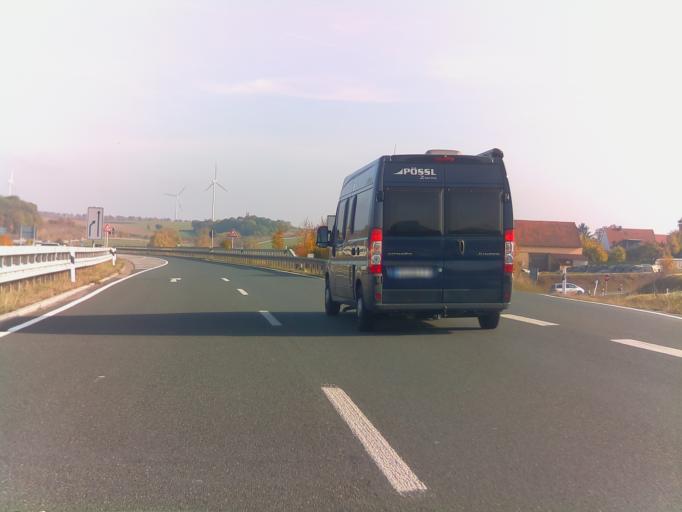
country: DE
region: Bavaria
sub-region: Regierungsbezirk Unterfranken
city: Biebelried
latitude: 49.7677
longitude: 10.0741
